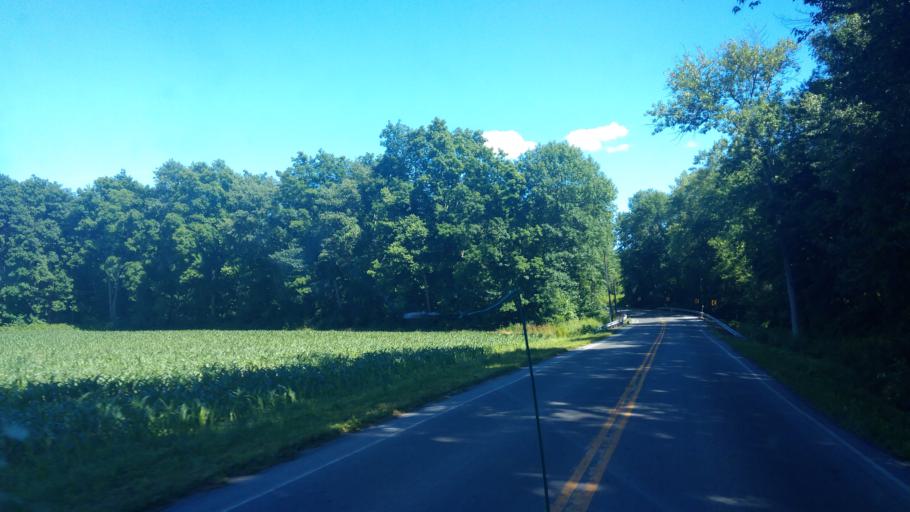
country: US
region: New York
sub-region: Wayne County
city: Lyons
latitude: 43.0235
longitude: -76.9424
